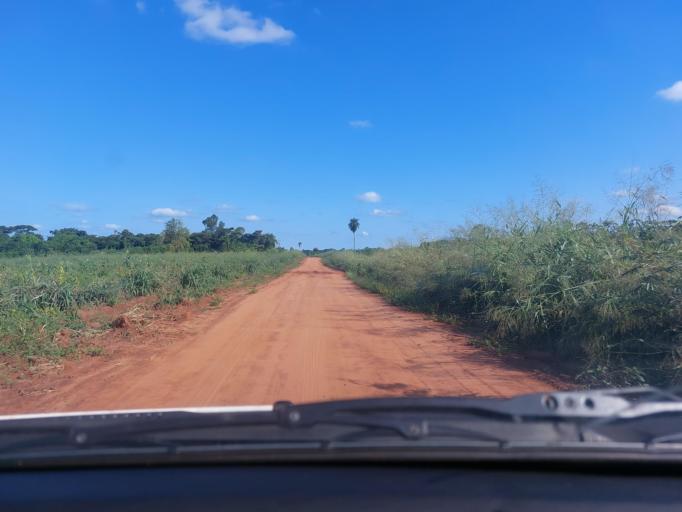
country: PY
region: San Pedro
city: Guayaybi
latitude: -24.5189
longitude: -56.5463
